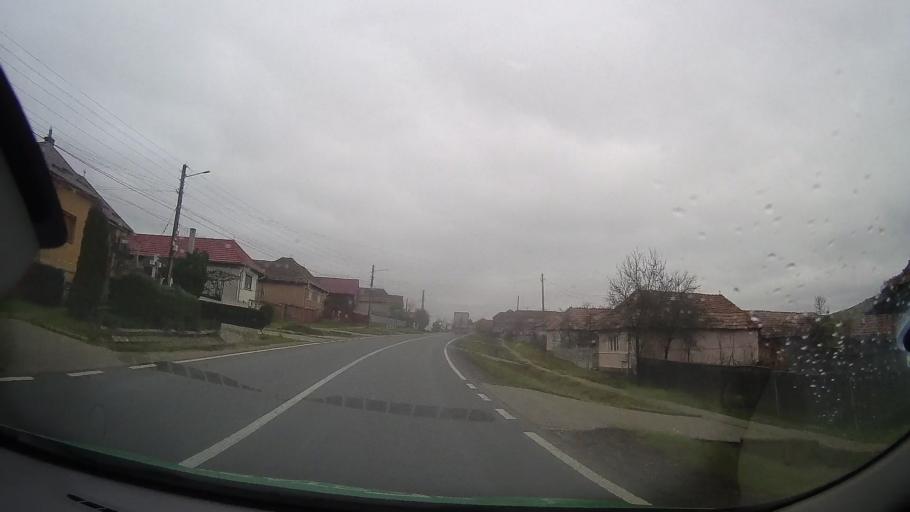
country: RO
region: Mures
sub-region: Comuna Lunca
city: Lunca
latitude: 46.8557
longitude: 24.5692
